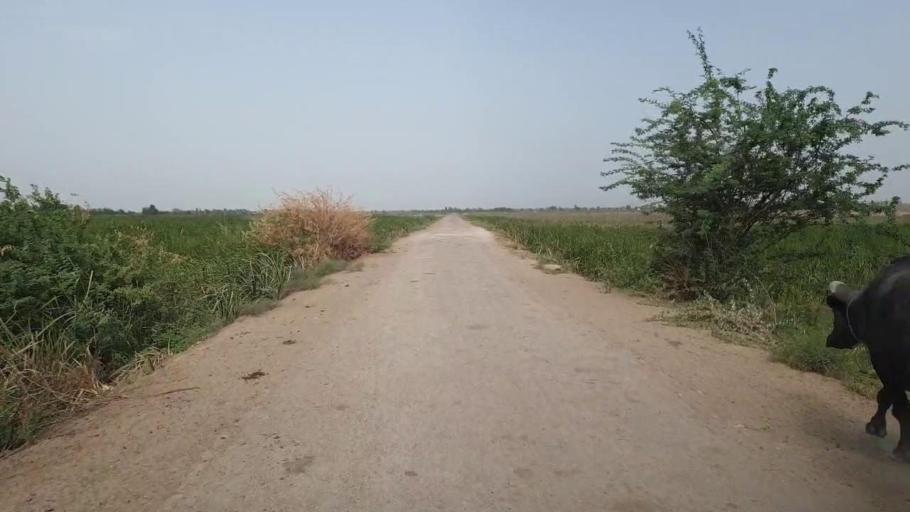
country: PK
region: Sindh
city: Daulatpur
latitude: 26.5463
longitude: 68.0783
